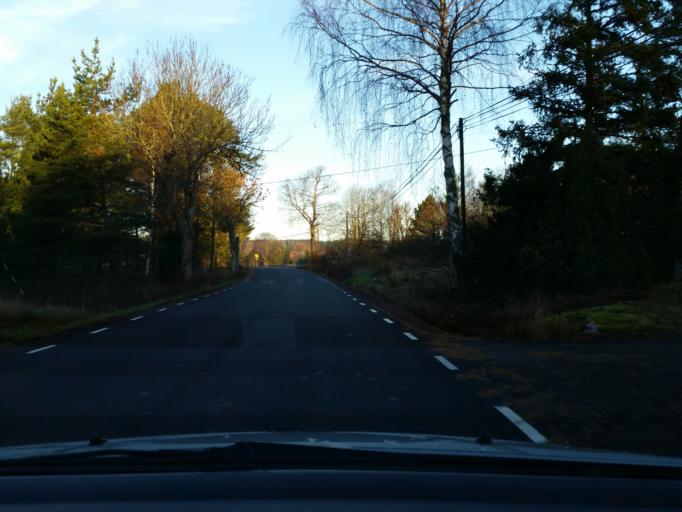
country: AX
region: Alands landsbygd
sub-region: Sund
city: Sund
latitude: 60.2388
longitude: 20.0723
